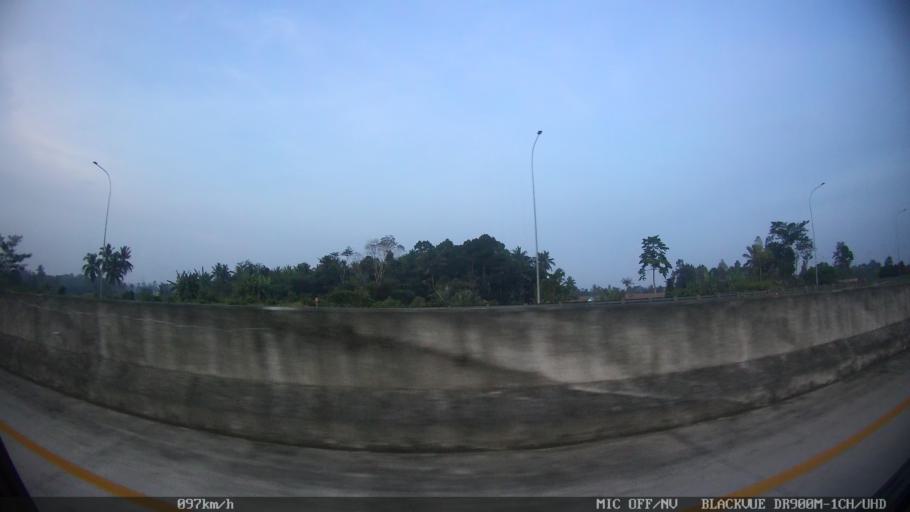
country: ID
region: Lampung
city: Pasuruan
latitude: -5.7244
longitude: 105.6669
